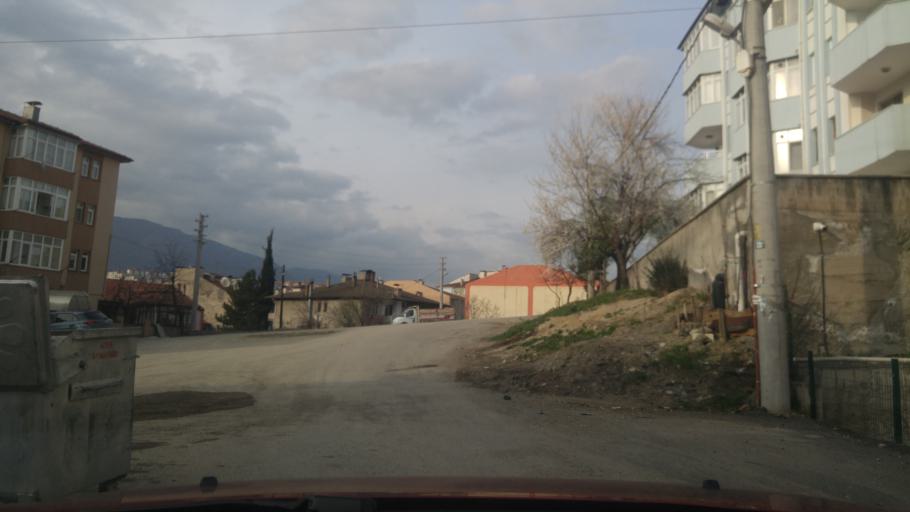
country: TR
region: Karabuk
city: Safranbolu
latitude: 41.2246
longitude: 32.6656
